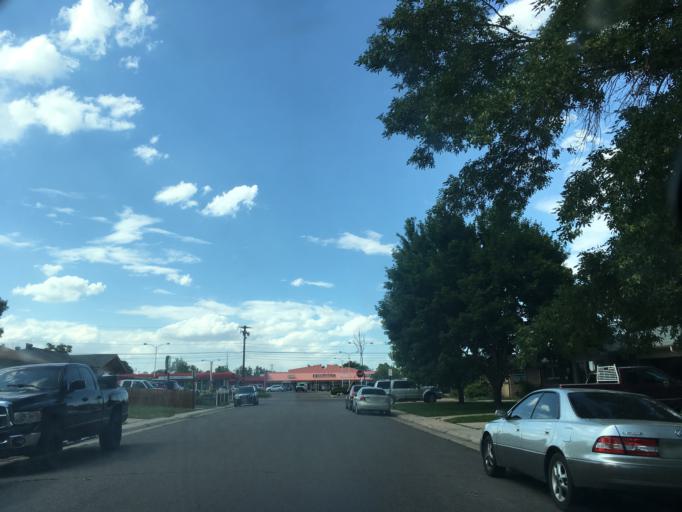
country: US
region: Colorado
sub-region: Jefferson County
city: Lakewood
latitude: 39.6888
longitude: -105.0433
